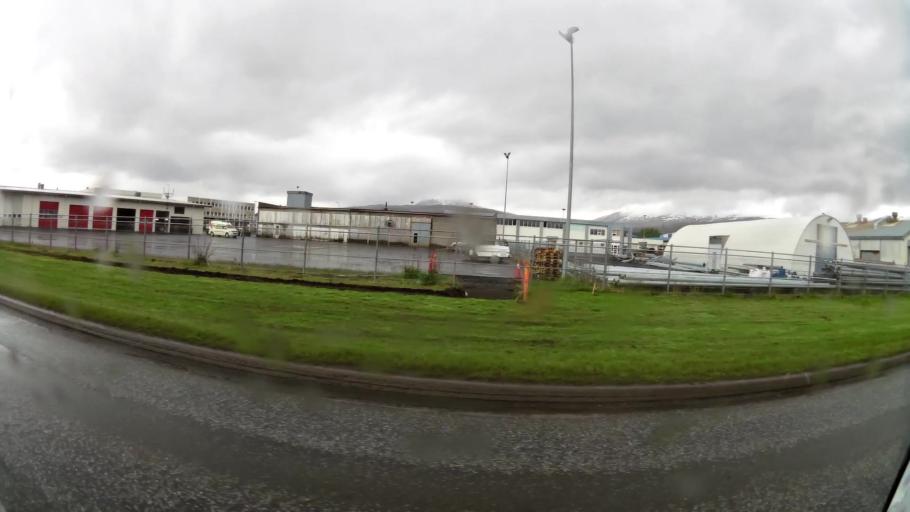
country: IS
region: Northeast
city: Akureyri
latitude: 65.6921
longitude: -18.0947
